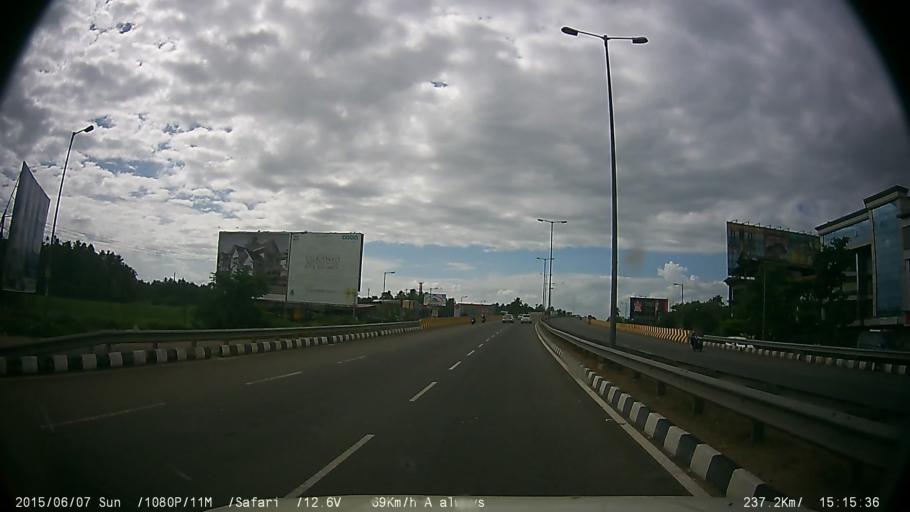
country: IN
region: Kerala
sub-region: Thrissur District
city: Trichur
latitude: 10.4463
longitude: 76.2589
